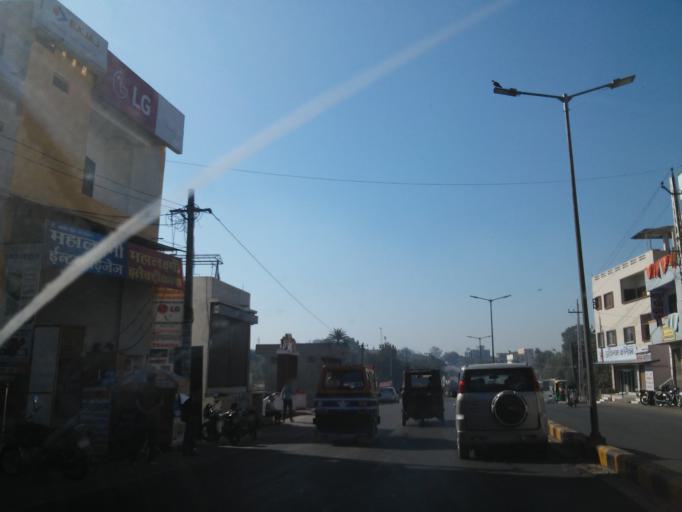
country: IN
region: Rajasthan
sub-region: Udaipur
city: Udaipur
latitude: 24.5460
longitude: 73.6870
